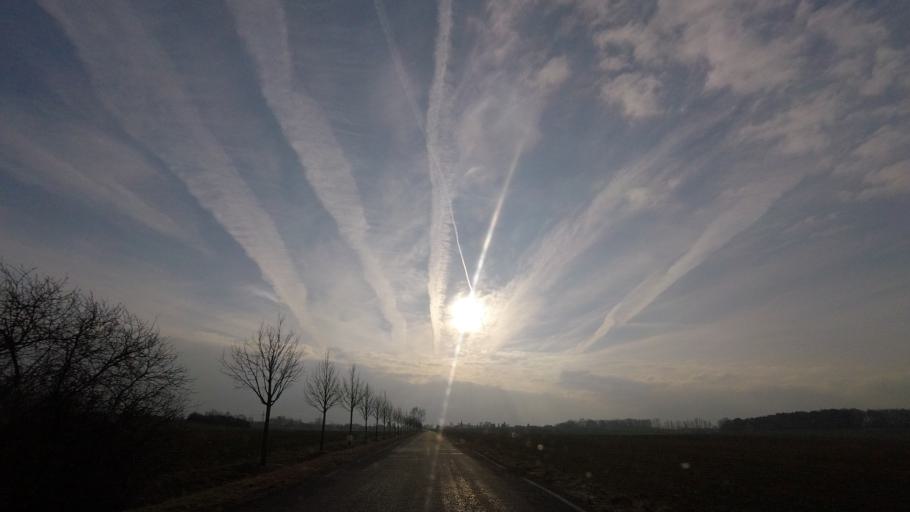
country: DE
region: Brandenburg
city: Belzig
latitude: 52.1176
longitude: 12.5475
